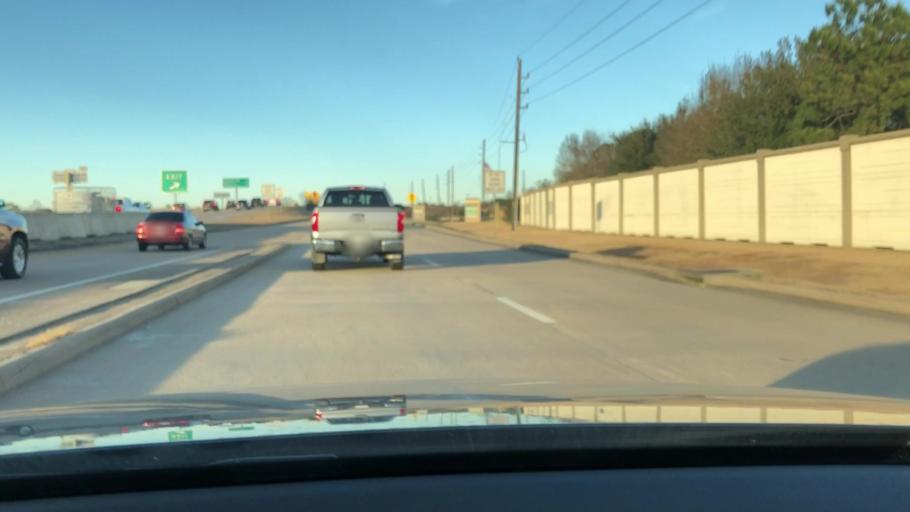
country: US
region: Texas
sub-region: Fort Bend County
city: Cinco Ranch
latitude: 29.7107
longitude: -95.7745
